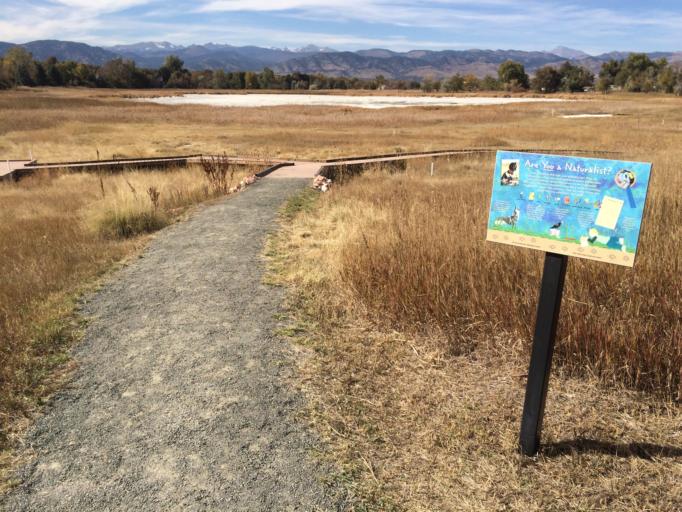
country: US
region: Colorado
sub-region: Boulder County
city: Gunbarrel
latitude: 40.0107
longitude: -105.2034
